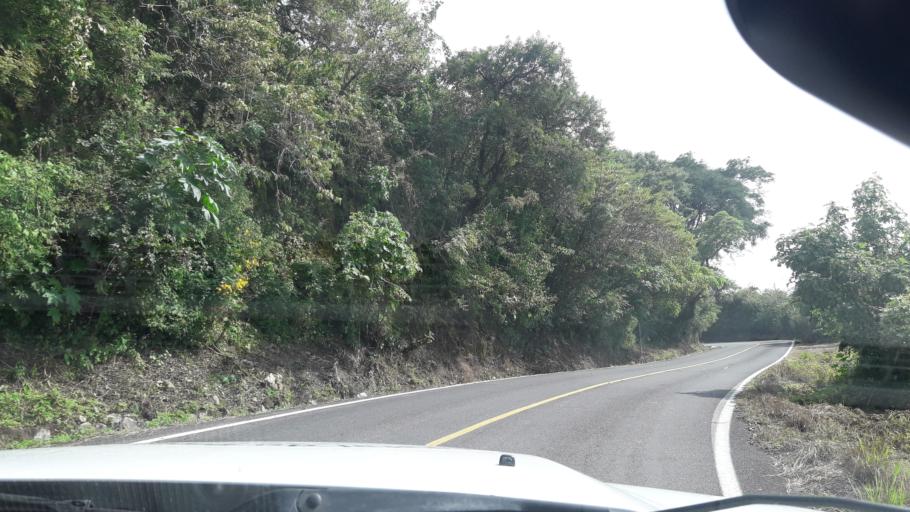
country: MX
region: Colima
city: Suchitlan
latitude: 19.4362
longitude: -103.7067
